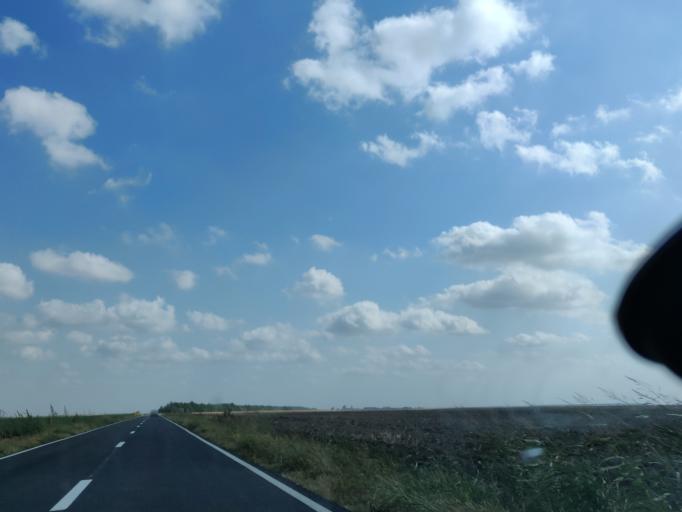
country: RO
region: Vrancea
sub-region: Comuna Ciorasti
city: Mihalceni
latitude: 45.4469
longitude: 27.3541
